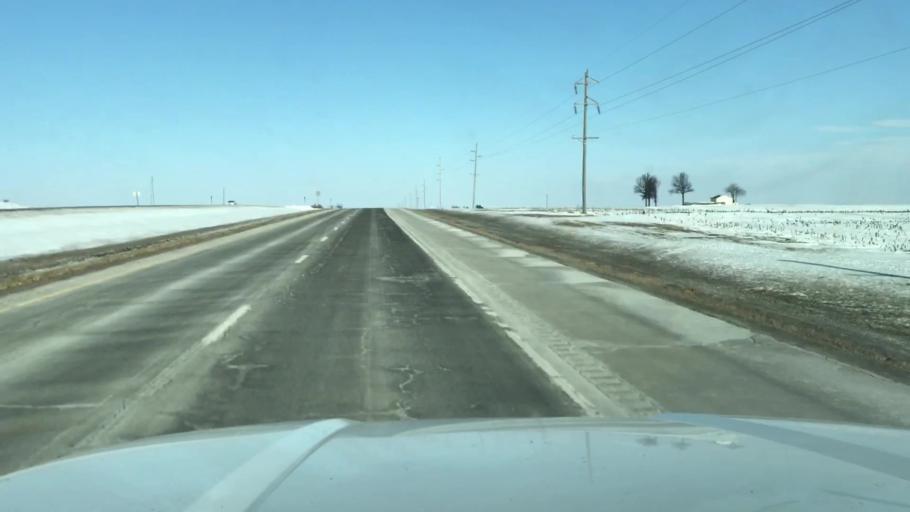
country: US
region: Missouri
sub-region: Nodaway County
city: Maryville
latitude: 40.2272
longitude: -94.8677
